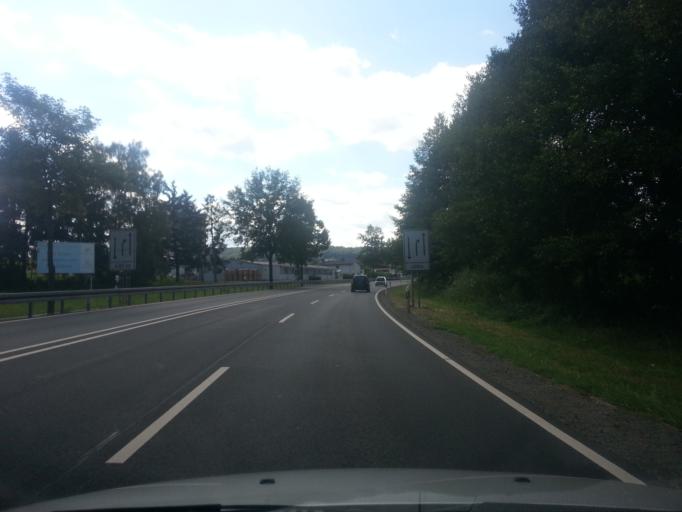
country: DE
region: Hesse
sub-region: Regierungsbezirk Darmstadt
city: Bad Konig
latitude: 49.7545
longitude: 9.0007
